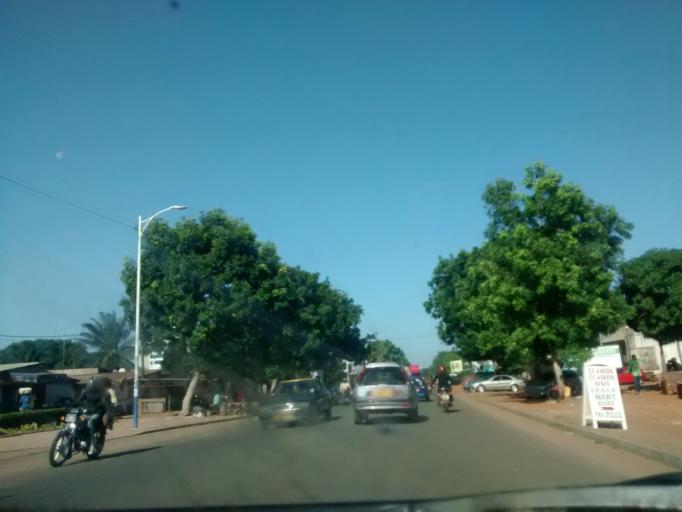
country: TG
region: Maritime
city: Lome
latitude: 6.1704
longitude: 1.1933
